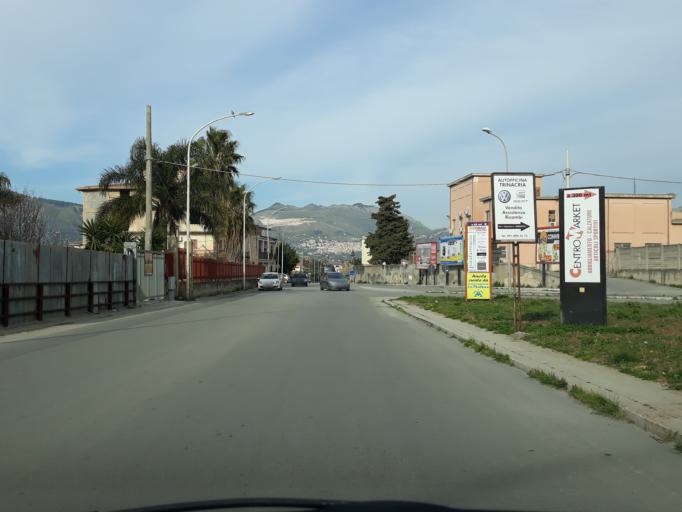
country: IT
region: Sicily
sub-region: Palermo
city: Partinico
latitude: 38.0536
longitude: 13.1275
